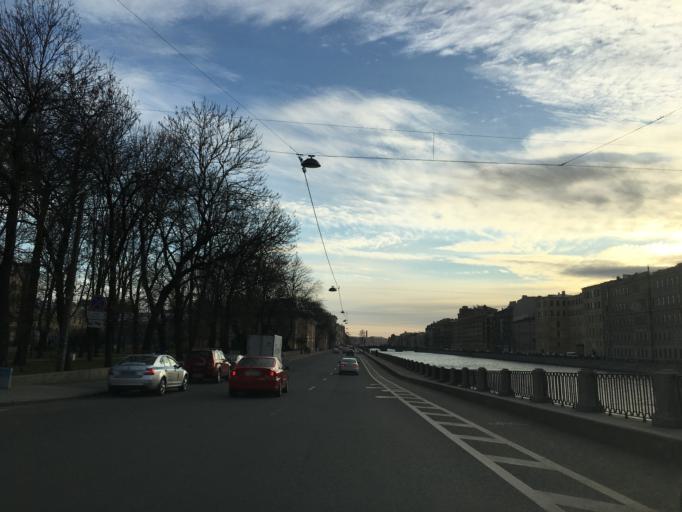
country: RU
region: St.-Petersburg
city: Saint Petersburg
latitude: 59.9212
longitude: 30.3174
